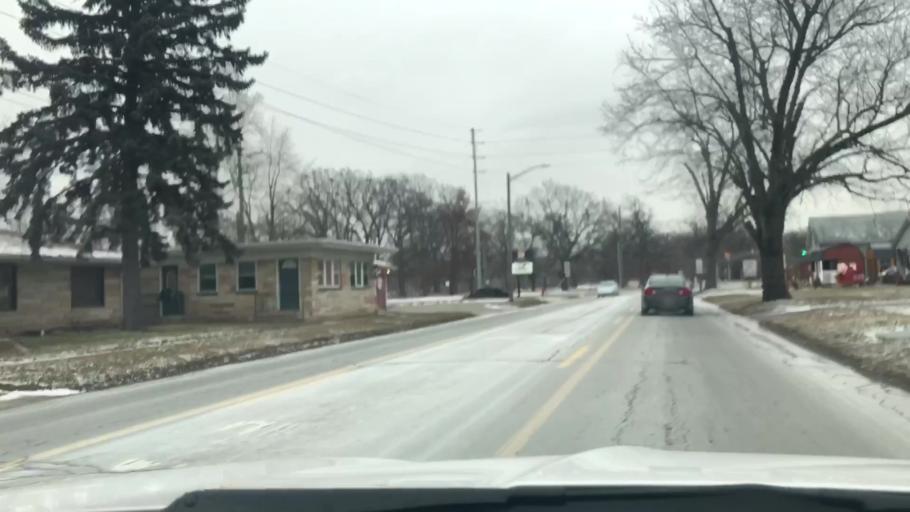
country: US
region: Indiana
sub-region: Fulton County
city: Rochester
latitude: 41.0645
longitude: -86.2075
